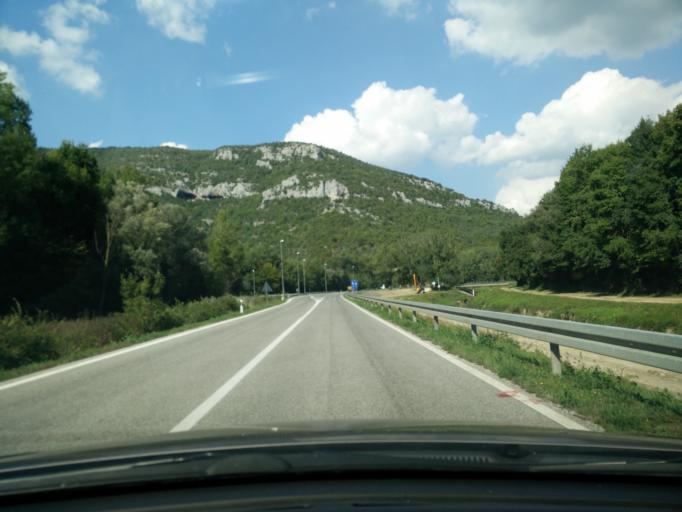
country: HR
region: Istarska
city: Buzet
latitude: 45.3751
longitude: 13.8891
